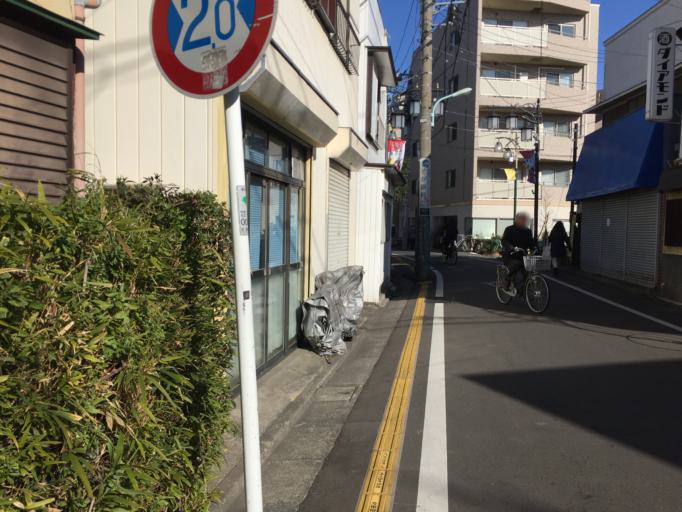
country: JP
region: Tokyo
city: Tokyo
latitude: 35.6557
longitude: 139.6485
